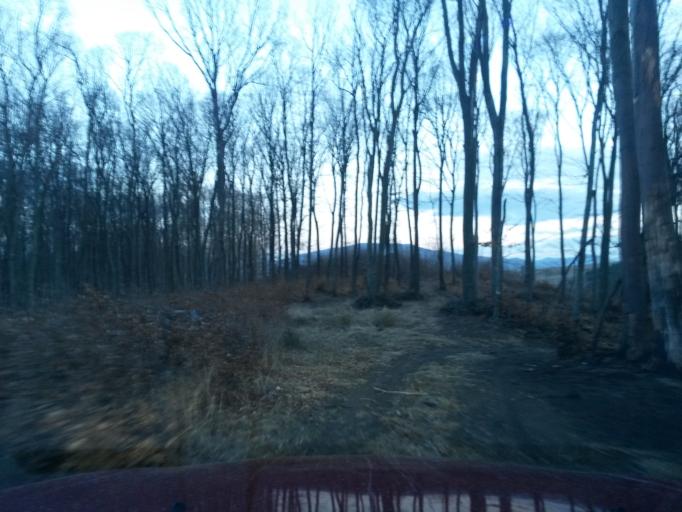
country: SK
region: Kosicky
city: Kosice
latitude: 48.7014
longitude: 21.3840
